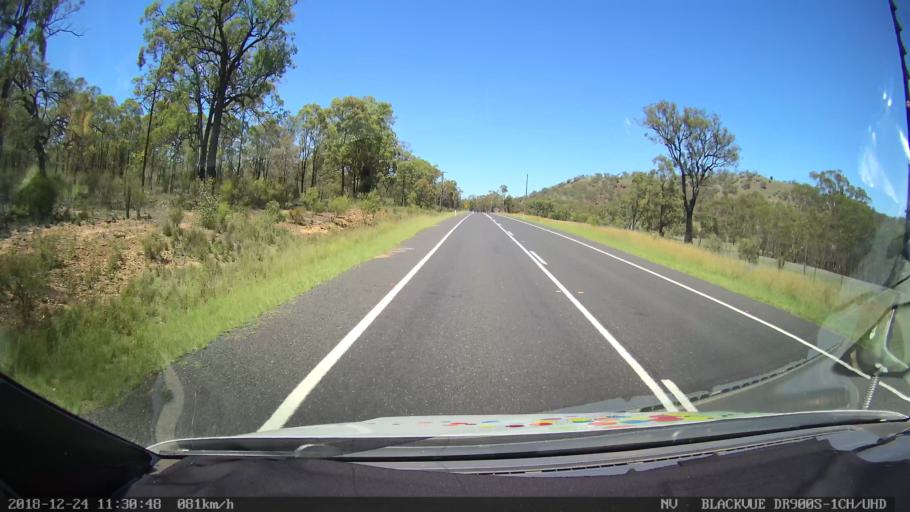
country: AU
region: New South Wales
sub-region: Upper Hunter Shire
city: Merriwa
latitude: -32.2086
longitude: 150.4635
